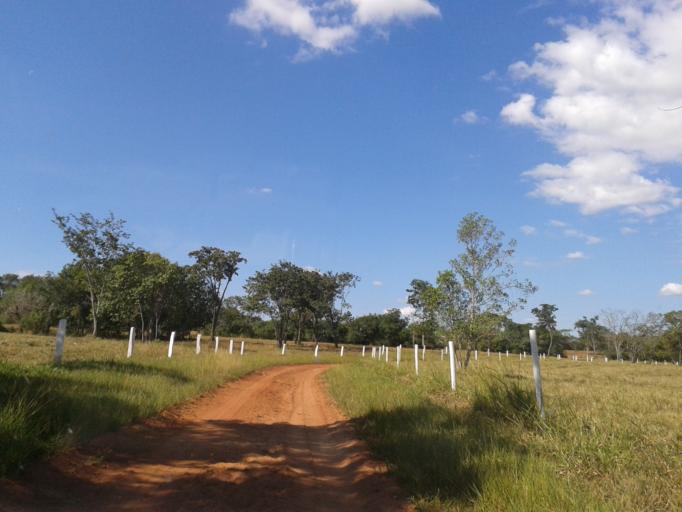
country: BR
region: Minas Gerais
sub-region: Campina Verde
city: Campina Verde
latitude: -19.3849
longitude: -49.7431
